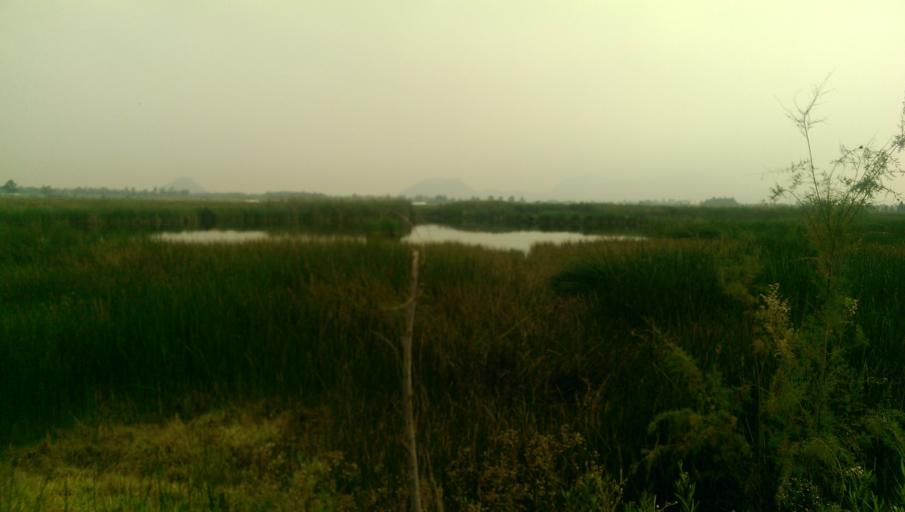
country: MX
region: Mexico City
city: Tlahuac
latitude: 19.2644
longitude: -99.0493
